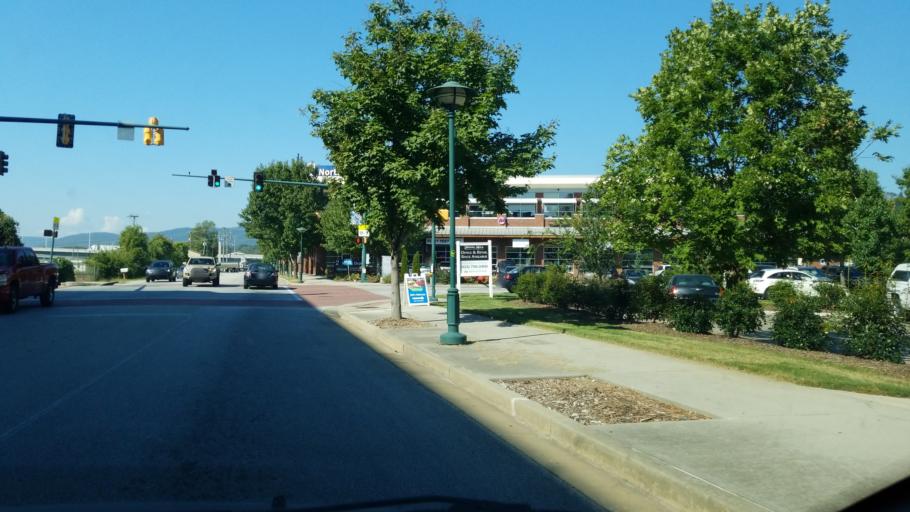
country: US
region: Tennessee
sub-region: Hamilton County
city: Chattanooga
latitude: 35.0626
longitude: -85.3131
